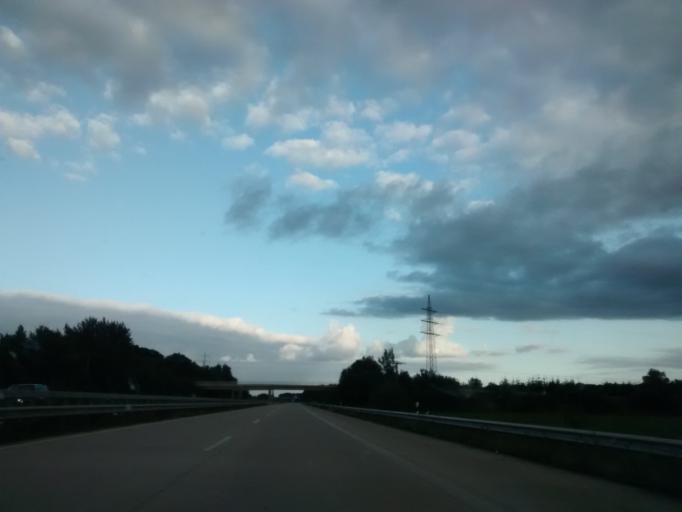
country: DE
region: Lower Saxony
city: Isterberg
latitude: 52.3363
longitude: 7.1160
